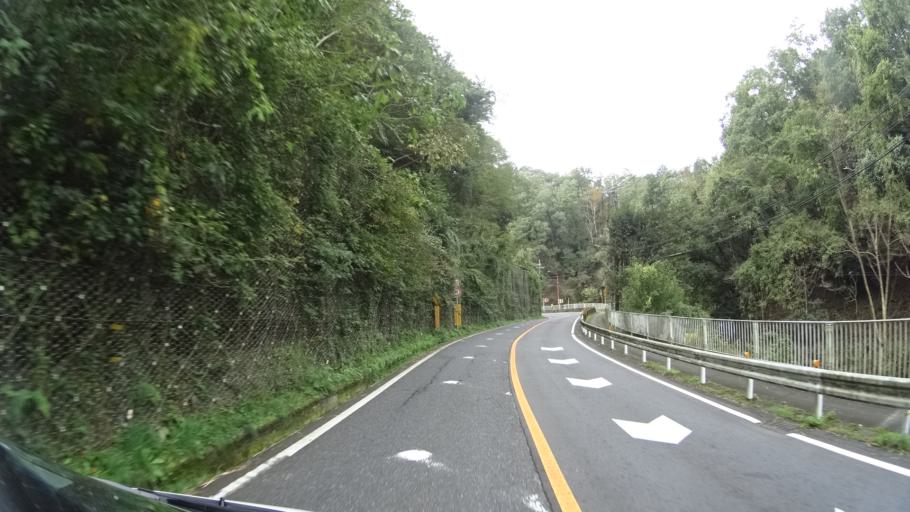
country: JP
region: Shiga Prefecture
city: Otsu-shi
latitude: 35.0393
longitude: 135.8272
